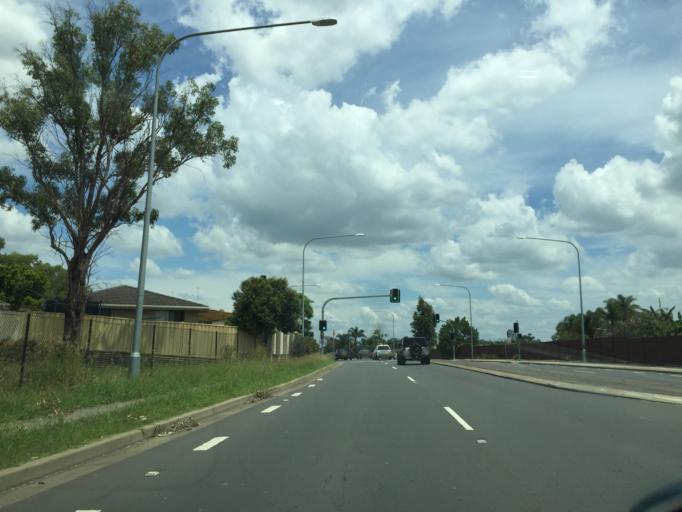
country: AU
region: New South Wales
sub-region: Blacktown
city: Hassall Grove
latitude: -33.7348
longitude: 150.8462
